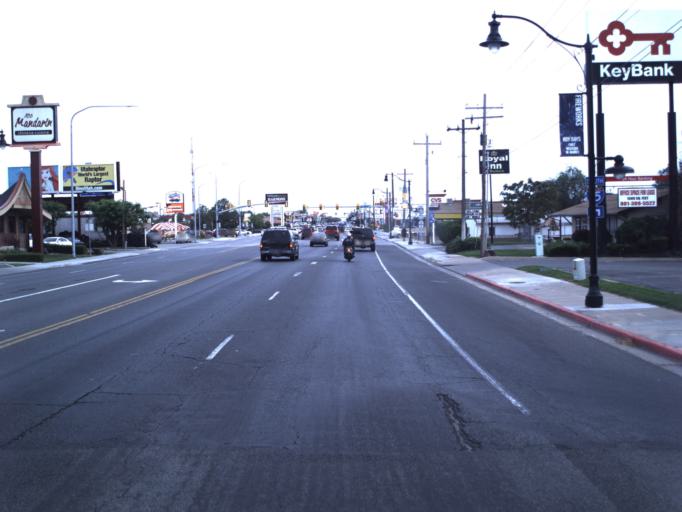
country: US
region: Utah
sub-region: Weber County
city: Roy
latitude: 41.1691
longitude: -112.0261
